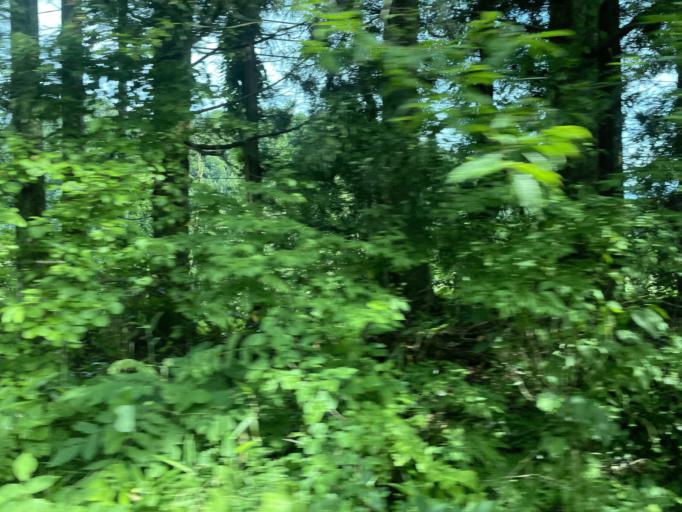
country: JP
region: Niigata
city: Suibara
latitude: 37.6882
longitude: 139.4562
